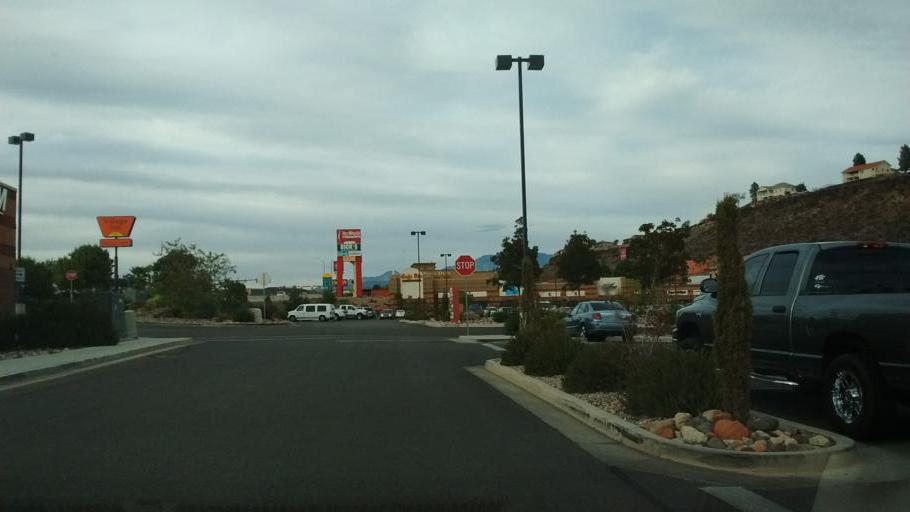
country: US
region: Utah
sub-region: Washington County
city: Saint George
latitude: 37.1074
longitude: -113.5544
